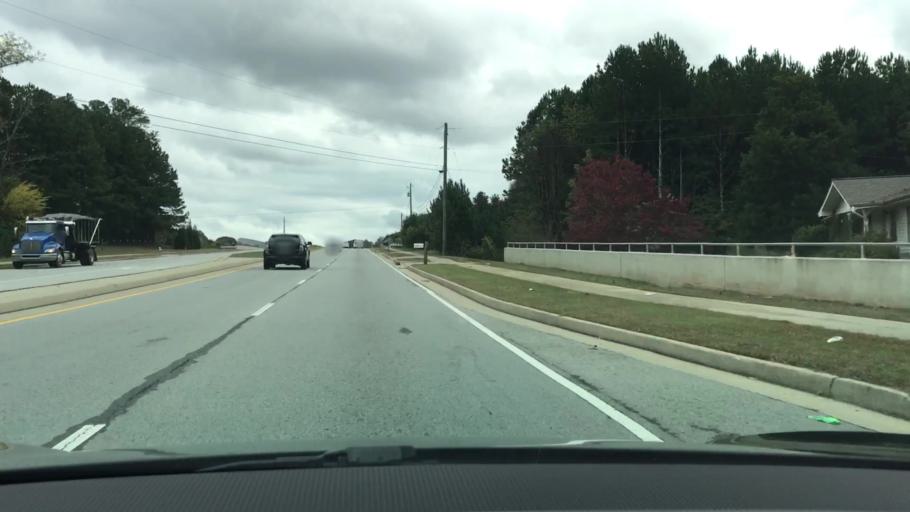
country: US
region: Georgia
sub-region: Gwinnett County
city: Suwanee
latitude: 34.0267
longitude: -84.0565
